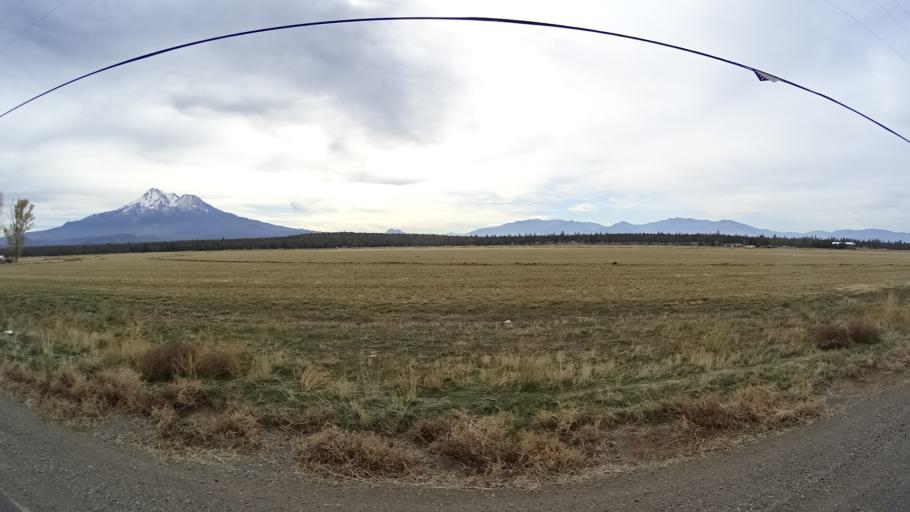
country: US
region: California
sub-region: Siskiyou County
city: Weed
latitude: 41.5959
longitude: -122.3333
